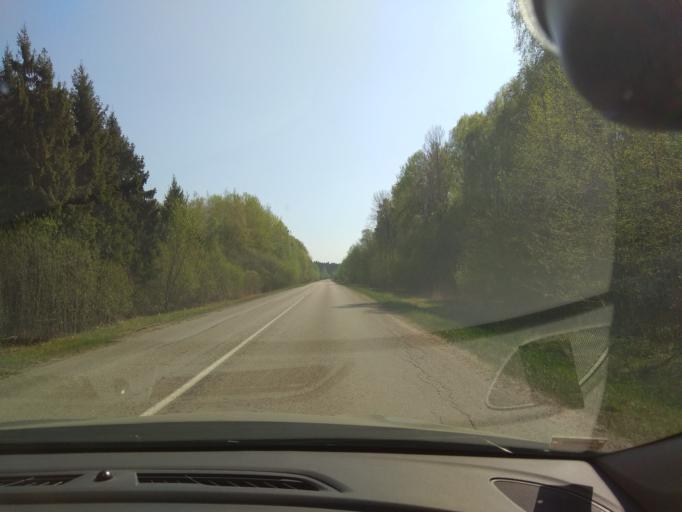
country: LT
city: Linkuva
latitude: 55.9948
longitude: 24.1716
